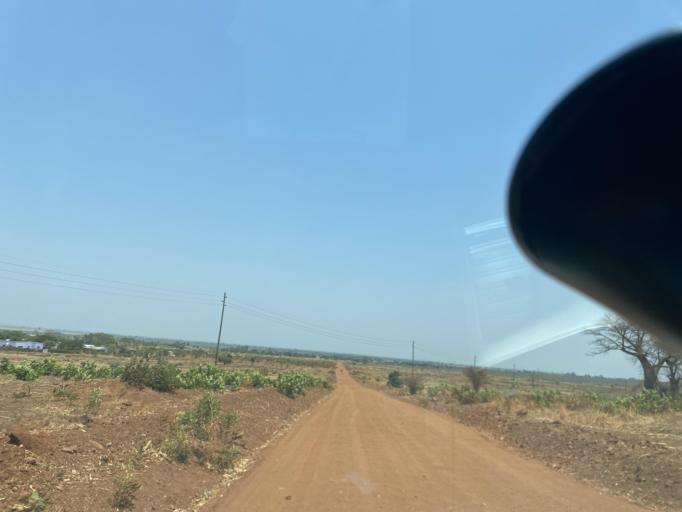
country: ZM
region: Southern
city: Nakambala
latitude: -15.5030
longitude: 27.9271
